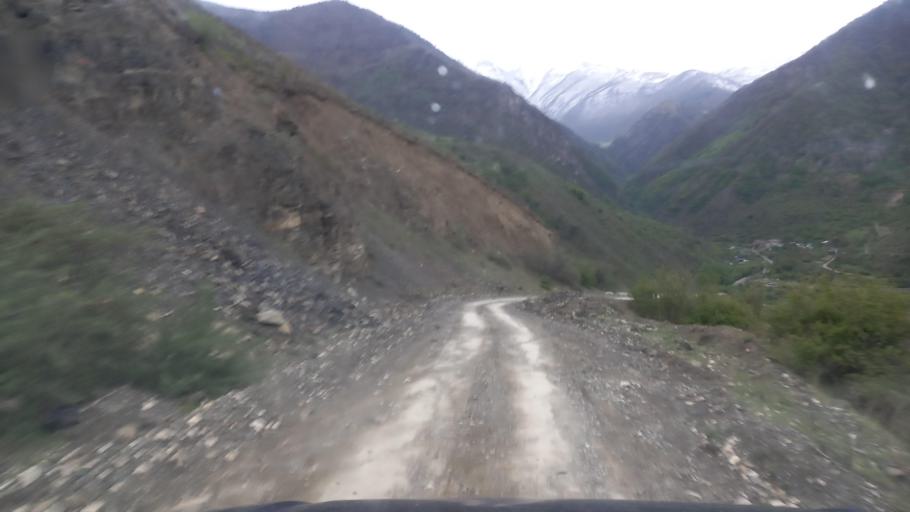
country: RU
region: North Ossetia
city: Mizur
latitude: 42.8568
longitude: 44.1577
